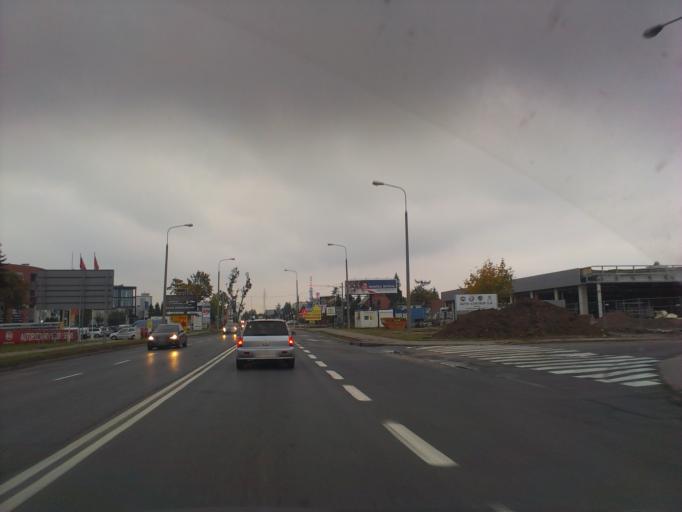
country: PL
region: Greater Poland Voivodeship
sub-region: Powiat poznanski
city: Suchy Las
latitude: 52.4449
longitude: 16.9087
